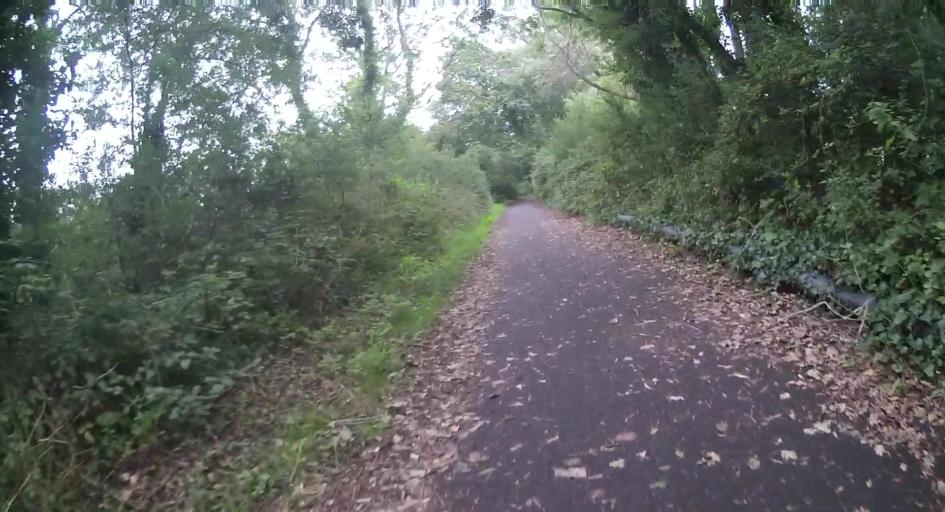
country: GB
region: England
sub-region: Isle of Wight
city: Sandown
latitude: 50.6622
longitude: -1.1638
